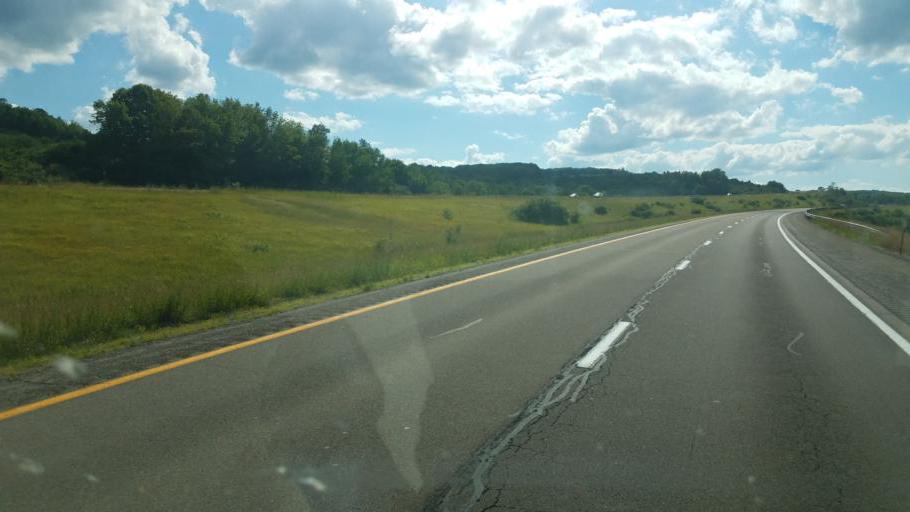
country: US
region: New York
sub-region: Allegany County
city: Alfred
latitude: 42.3181
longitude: -77.8191
